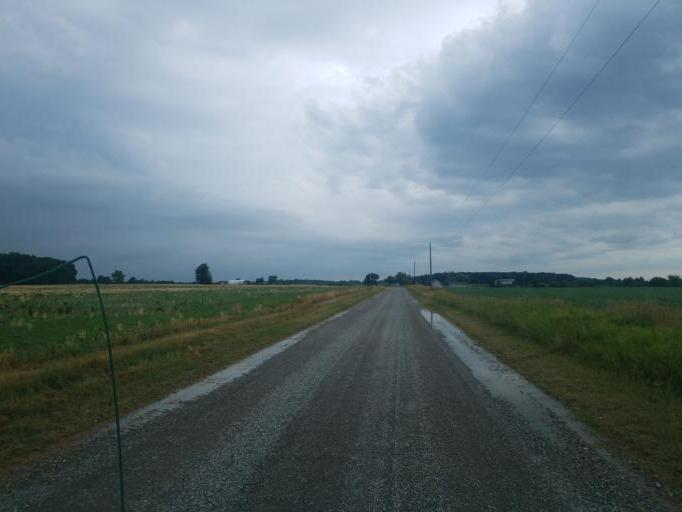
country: US
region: Ohio
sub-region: Defiance County
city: Hicksville
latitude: 41.3181
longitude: -84.8039
